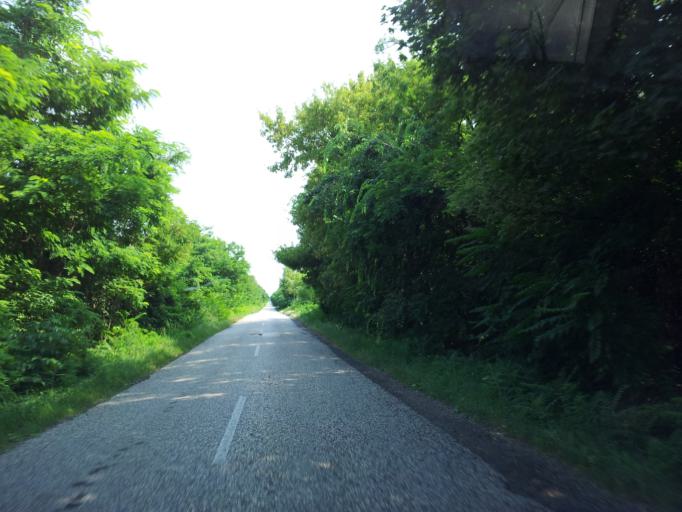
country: HU
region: Pest
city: Szigetujfalu
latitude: 47.2051
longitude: 18.9125
